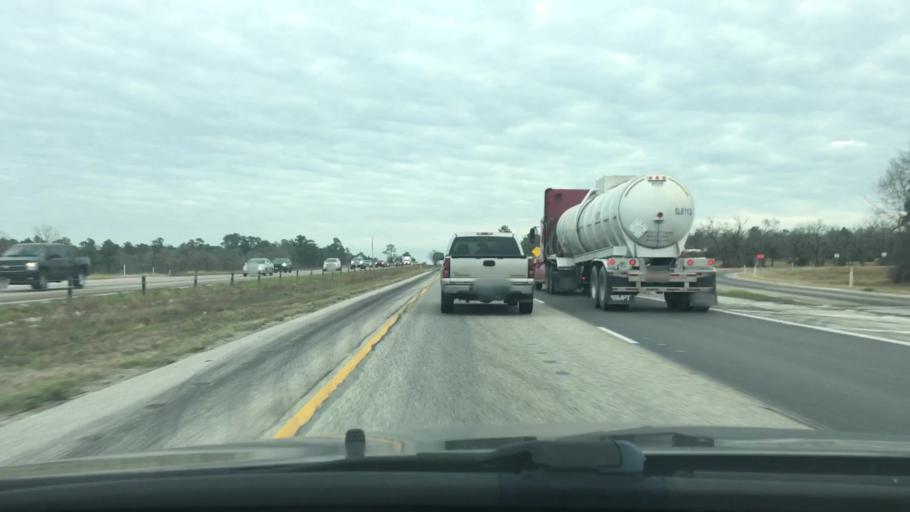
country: US
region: Texas
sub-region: Walker County
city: Huntsville
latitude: 30.7782
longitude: -95.6528
